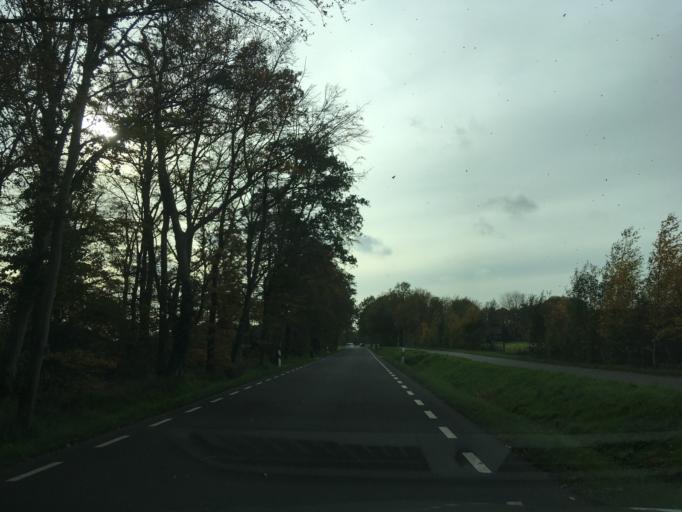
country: DE
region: North Rhine-Westphalia
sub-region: Regierungsbezirk Munster
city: Vreden
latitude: 52.0543
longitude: 6.8670
